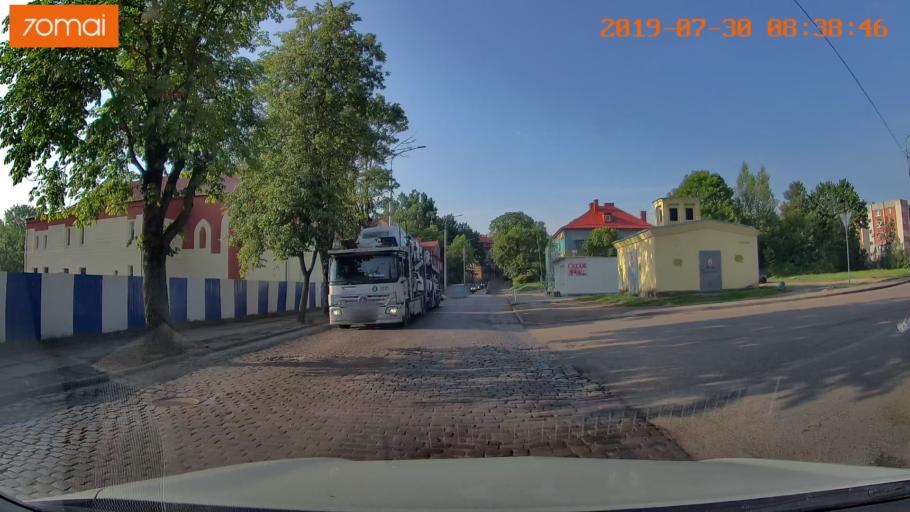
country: RU
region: Kaliningrad
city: Chernyakhovsk
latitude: 54.6333
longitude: 21.8030
